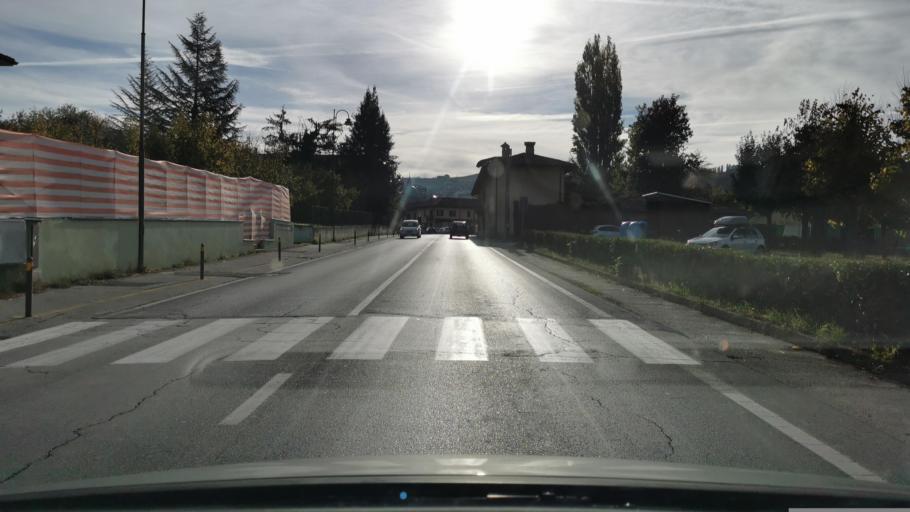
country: IT
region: Piedmont
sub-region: Provincia di Cuneo
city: Dogliani
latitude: 44.5336
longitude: 7.9394
